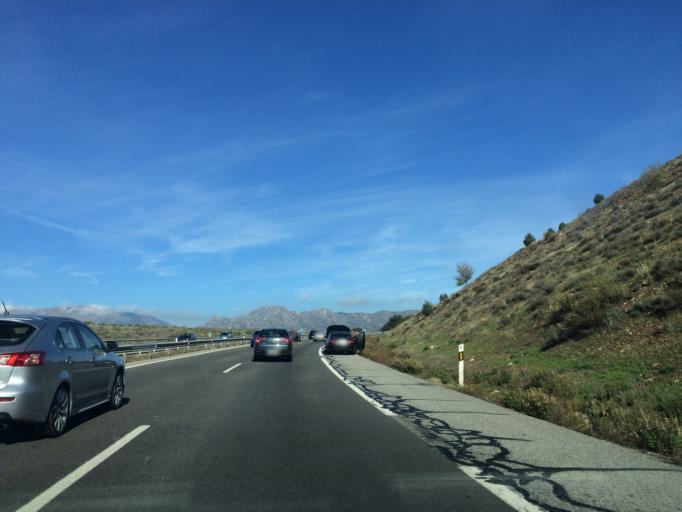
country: ES
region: Madrid
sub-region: Provincia de Madrid
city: Venturada
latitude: 40.8065
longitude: -3.6196
